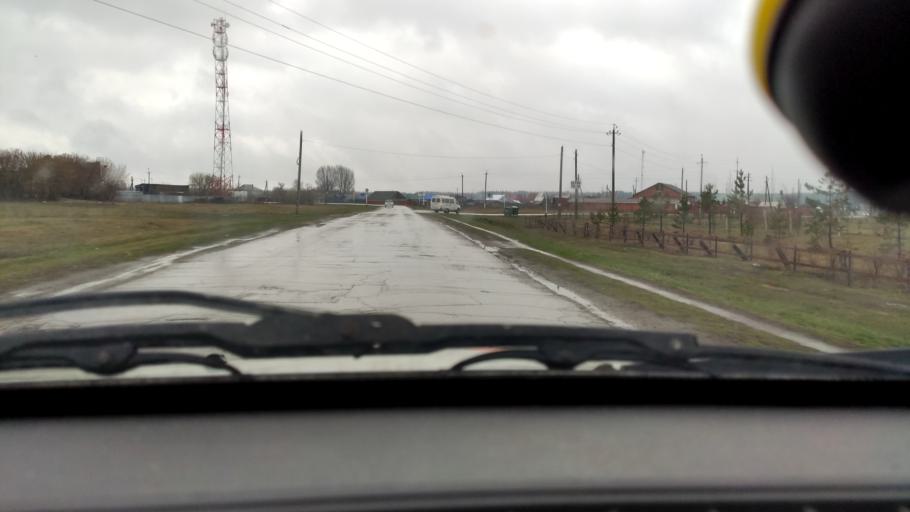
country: RU
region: Samara
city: Povolzhskiy
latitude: 53.6469
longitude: 49.6809
